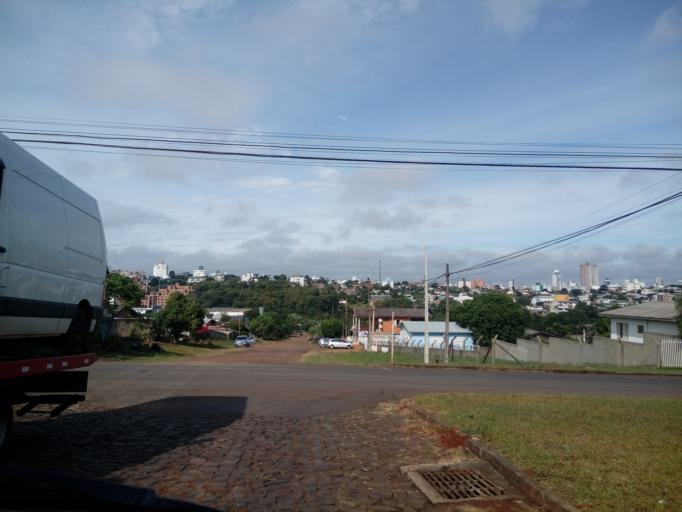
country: BR
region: Santa Catarina
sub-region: Chapeco
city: Chapeco
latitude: -27.0830
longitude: -52.6048
